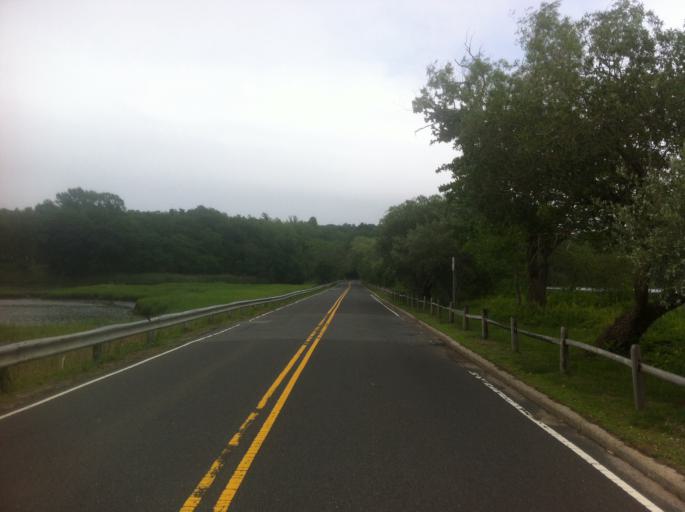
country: US
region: New York
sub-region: Nassau County
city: Locust Valley
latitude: 40.8856
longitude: -73.5774
